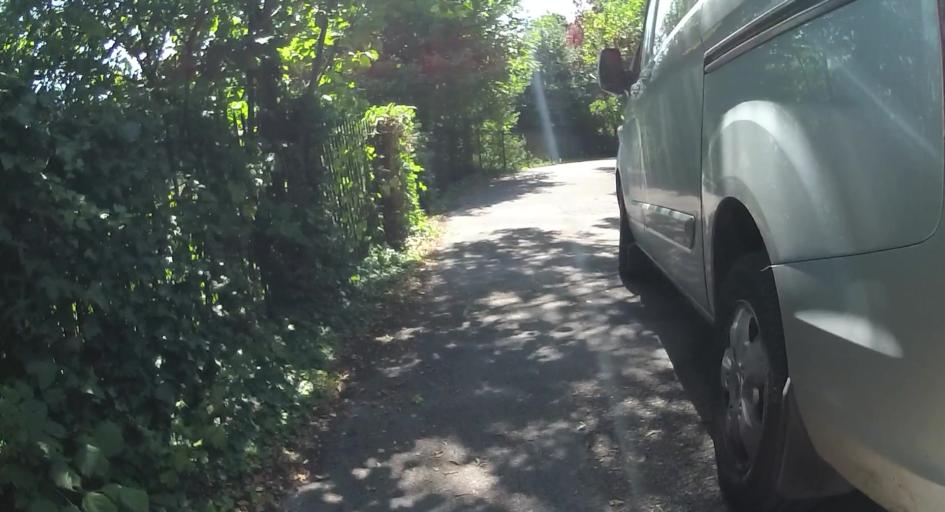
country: GB
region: England
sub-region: Hampshire
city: Winchester
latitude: 51.0484
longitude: -1.3215
